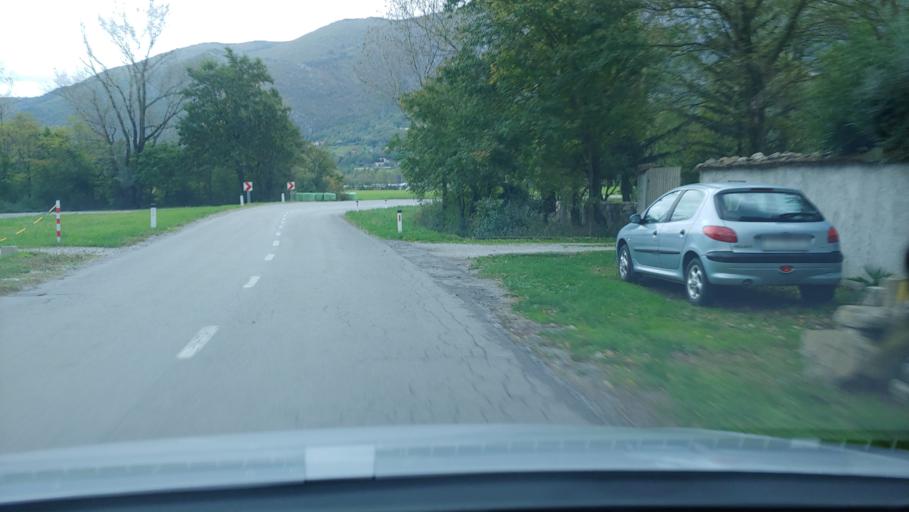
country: SI
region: Vipava
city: Vipava
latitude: 45.8253
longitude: 13.9487
